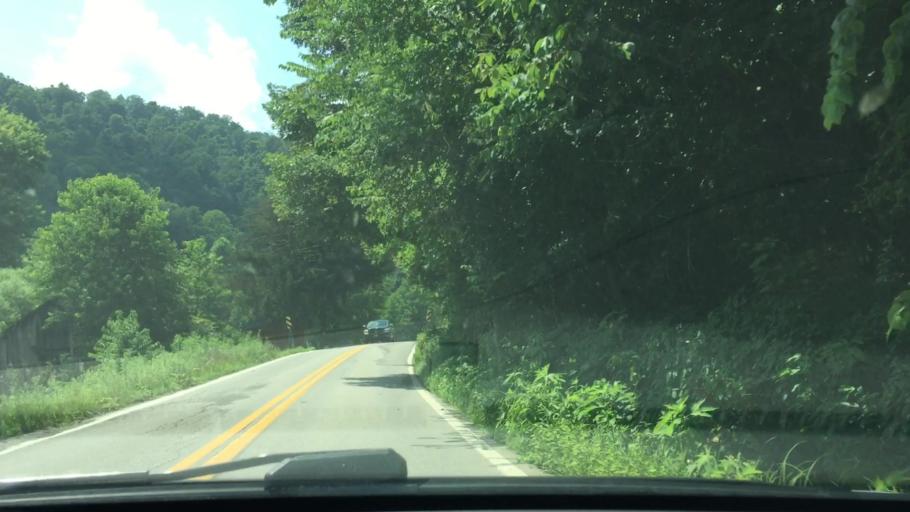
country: US
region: West Virginia
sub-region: Wetzel County
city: New Martinsville
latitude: 39.6891
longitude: -80.7953
